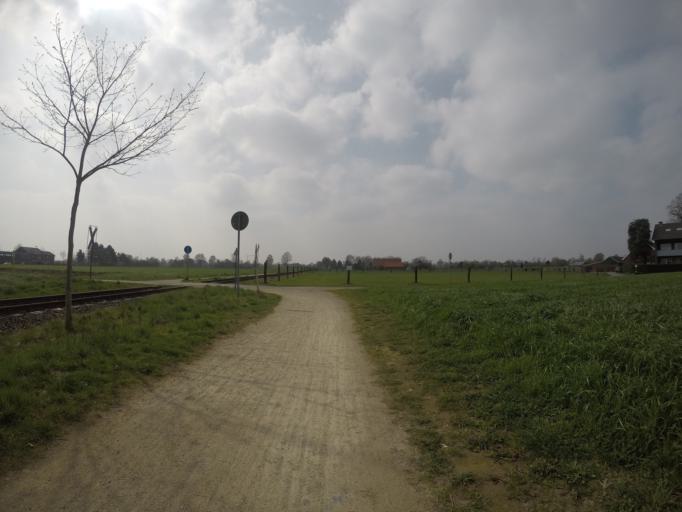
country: DE
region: North Rhine-Westphalia
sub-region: Regierungsbezirk Dusseldorf
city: Bocholt
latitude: 51.8185
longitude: 6.5906
